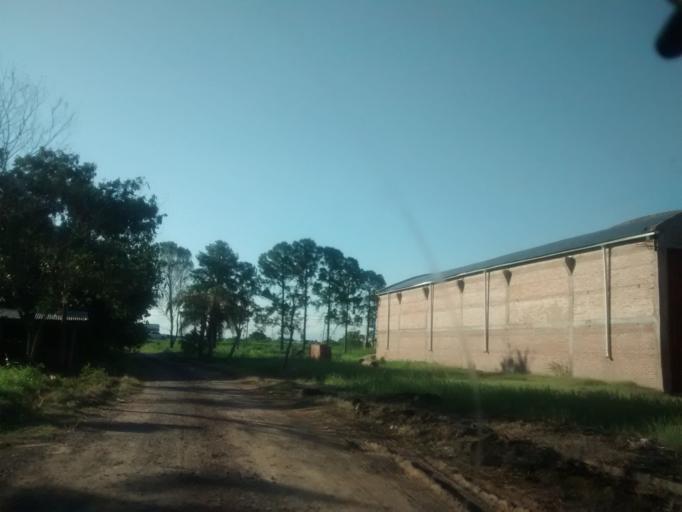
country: AR
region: Chaco
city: Fontana
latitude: -27.4626
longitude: -59.0397
